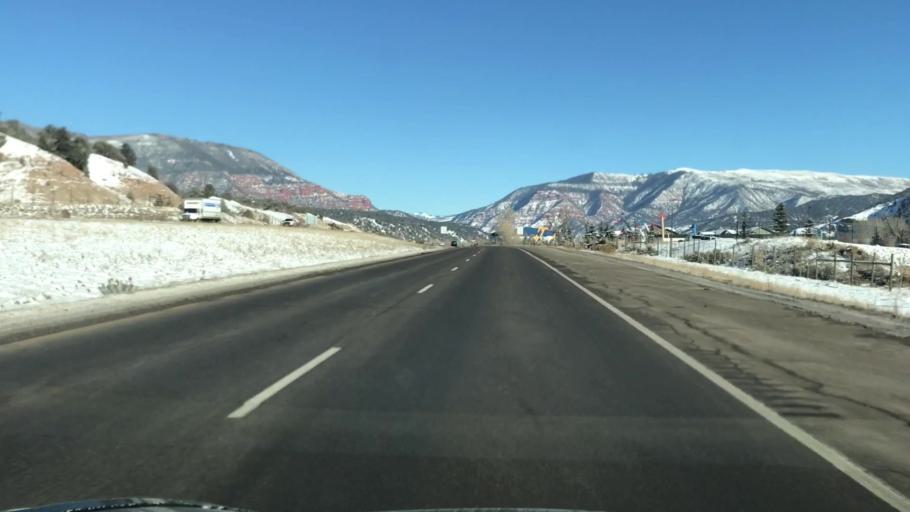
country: US
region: Colorado
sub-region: Eagle County
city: Eagle
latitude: 39.6647
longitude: -106.8186
